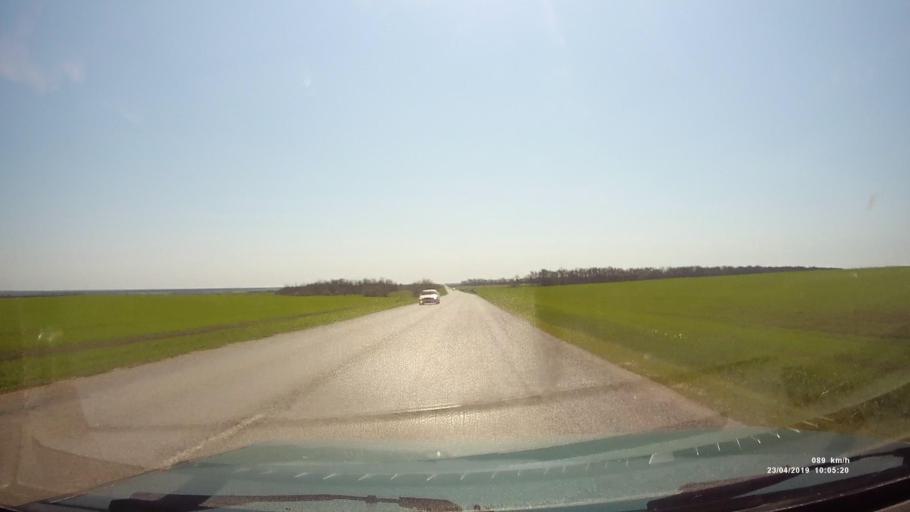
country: RU
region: Rostov
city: Sovetskoye
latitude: 46.7419
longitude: 42.2181
